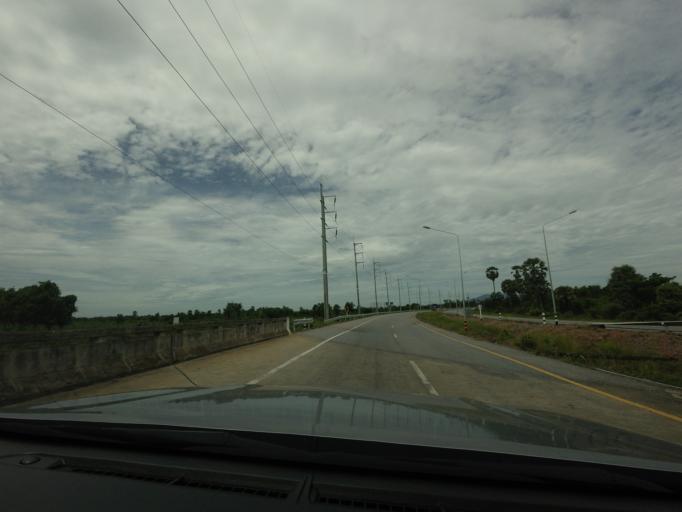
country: TH
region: Pattani
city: Pattani
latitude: 6.8413
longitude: 101.2252
